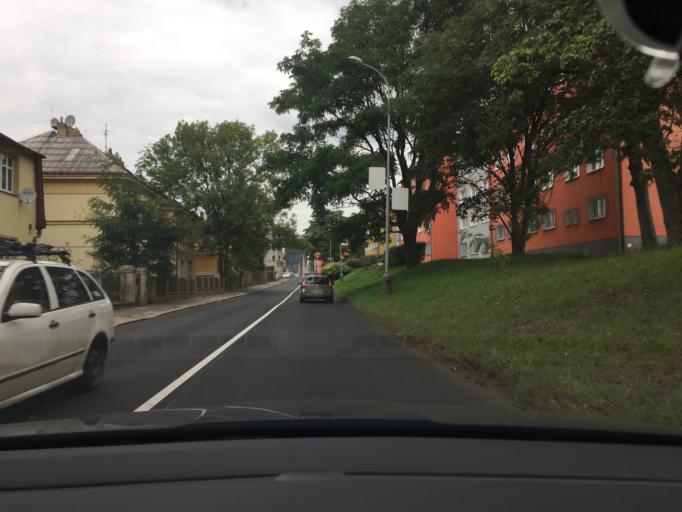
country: CZ
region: Ustecky
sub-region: Okres Usti nad Labem
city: Usti nad Labem
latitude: 50.6486
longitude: 14.0469
